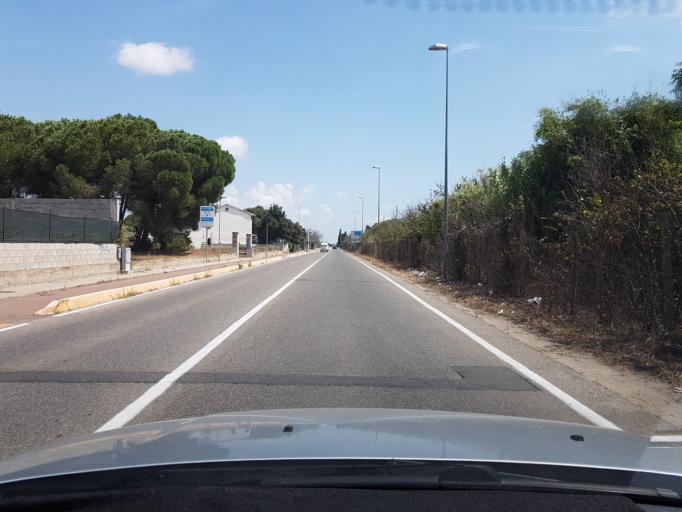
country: IT
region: Sardinia
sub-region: Provincia di Oristano
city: Oristano
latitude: 39.9106
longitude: 8.6052
